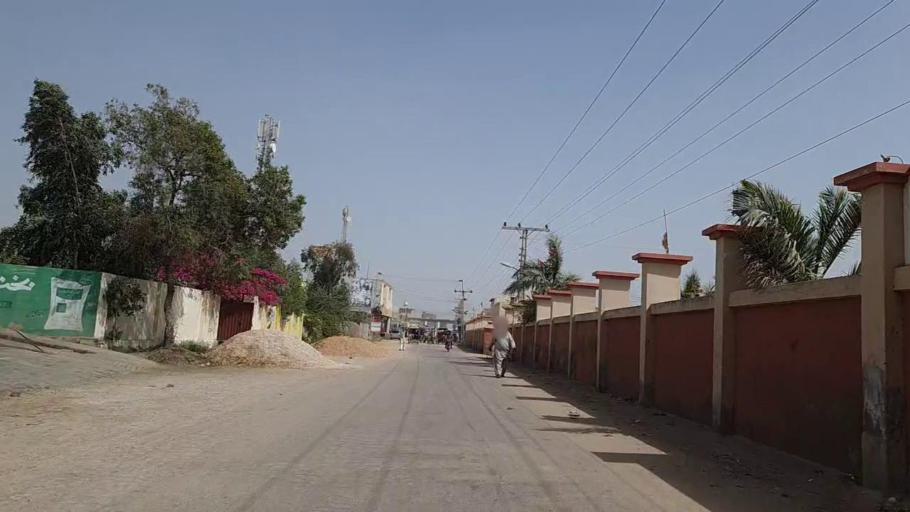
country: PK
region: Sindh
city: Tando Bago
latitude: 24.7870
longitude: 68.9634
